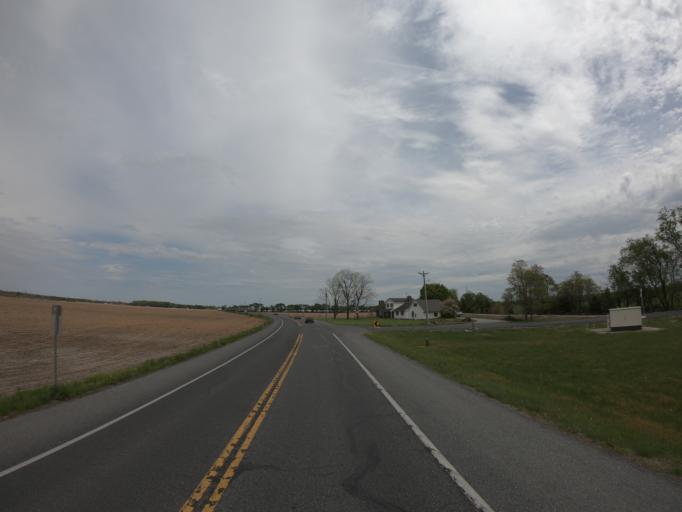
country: US
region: Delaware
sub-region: Sussex County
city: Milton
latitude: 38.7849
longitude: -75.3577
